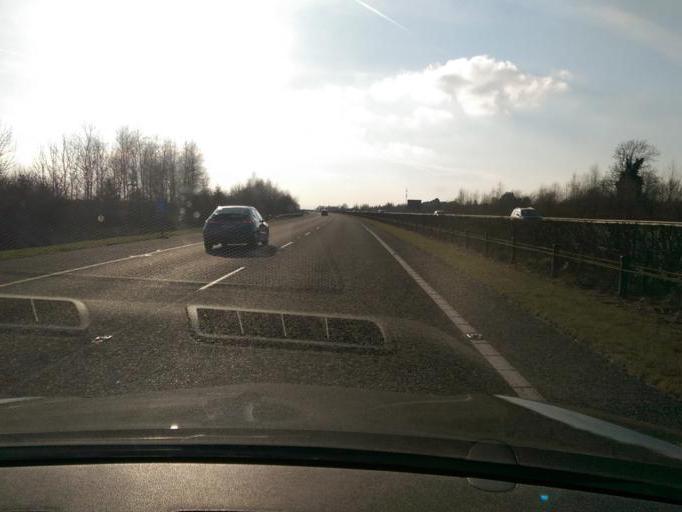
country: IE
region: Leinster
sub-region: Kildare
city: Cherryville
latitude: 53.1545
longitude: -6.9526
